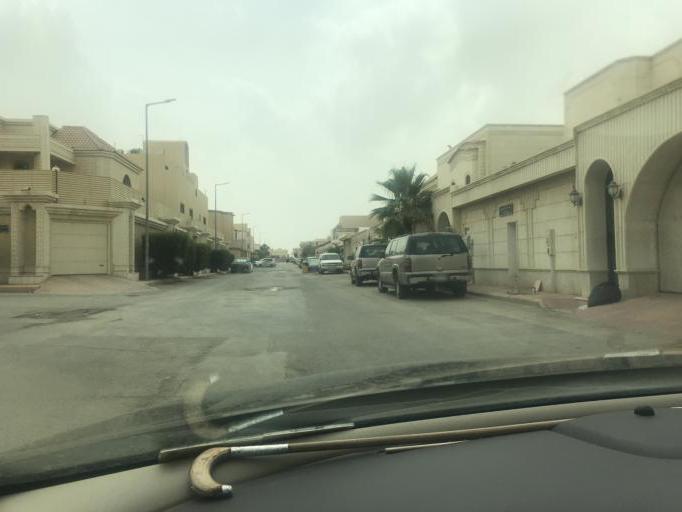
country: SA
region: Ar Riyad
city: Riyadh
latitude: 24.7358
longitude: 46.7884
